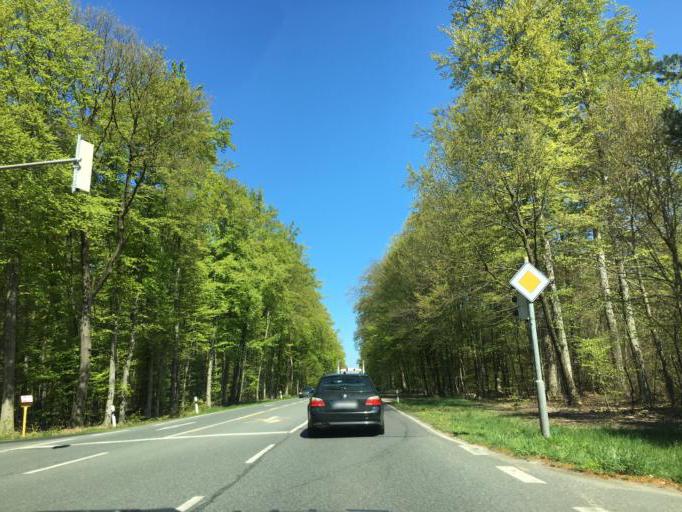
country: DE
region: Hesse
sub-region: Regierungsbezirk Darmstadt
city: Neu Isenburg
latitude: 50.0390
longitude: 8.7111
